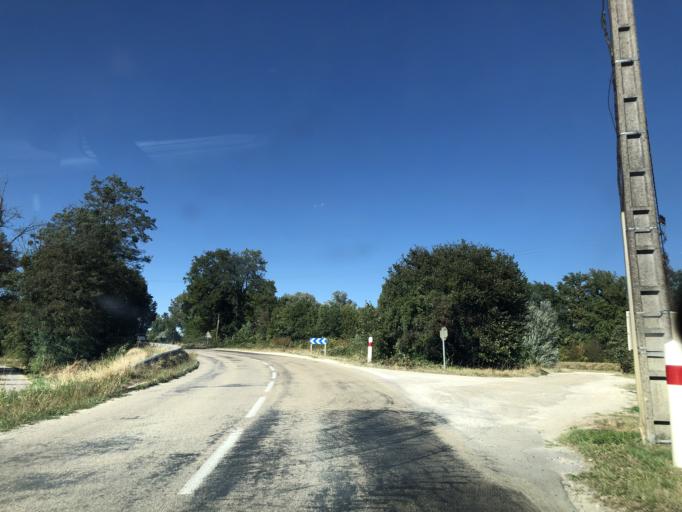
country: FR
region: Bourgogne
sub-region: Departement de l'Yonne
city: Appoigny
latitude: 47.8851
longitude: 3.5430
